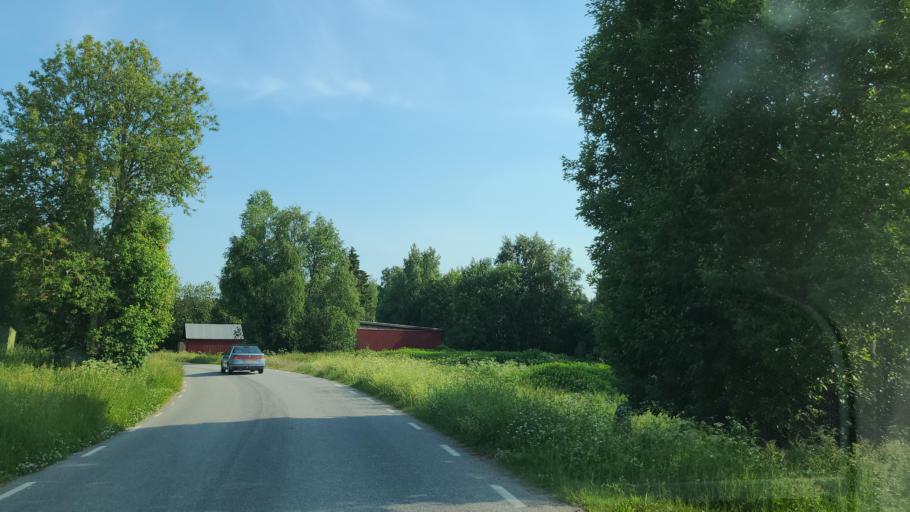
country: SE
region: Vaesterbotten
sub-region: Skelleftea Kommun
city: Burea
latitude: 64.3487
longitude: 21.3370
